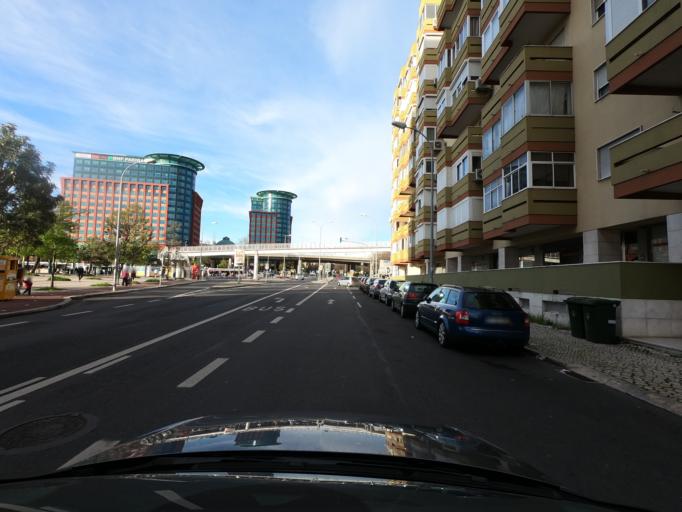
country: PT
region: Lisbon
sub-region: Odivelas
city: Pontinha
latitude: 38.7518
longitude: -9.1898
